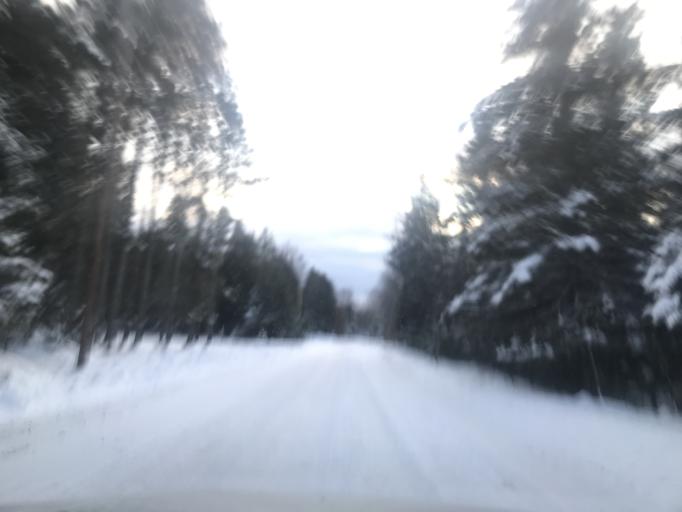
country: US
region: Michigan
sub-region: Delta County
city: Escanaba
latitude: 45.4217
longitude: -87.3335
